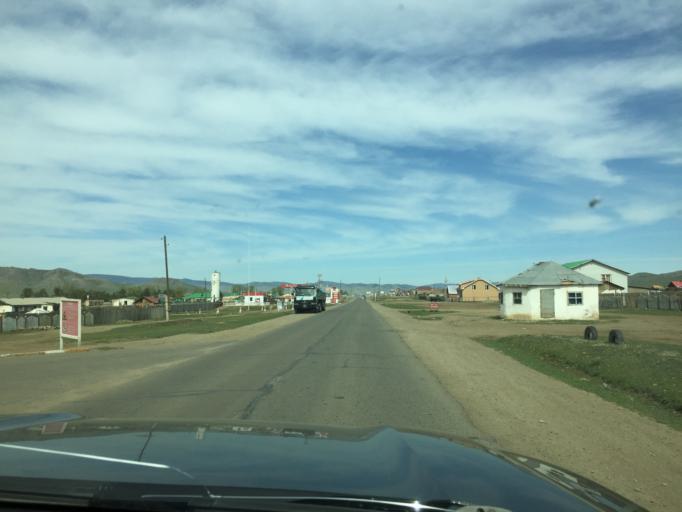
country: MN
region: Central Aimak
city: Ihsueuej
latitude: 48.2207
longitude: 106.2997
